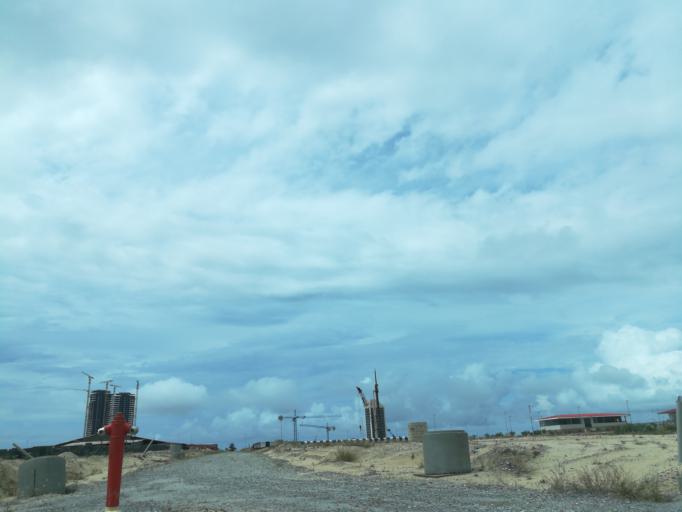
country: NG
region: Lagos
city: Lagos
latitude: 6.4137
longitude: 3.4090
